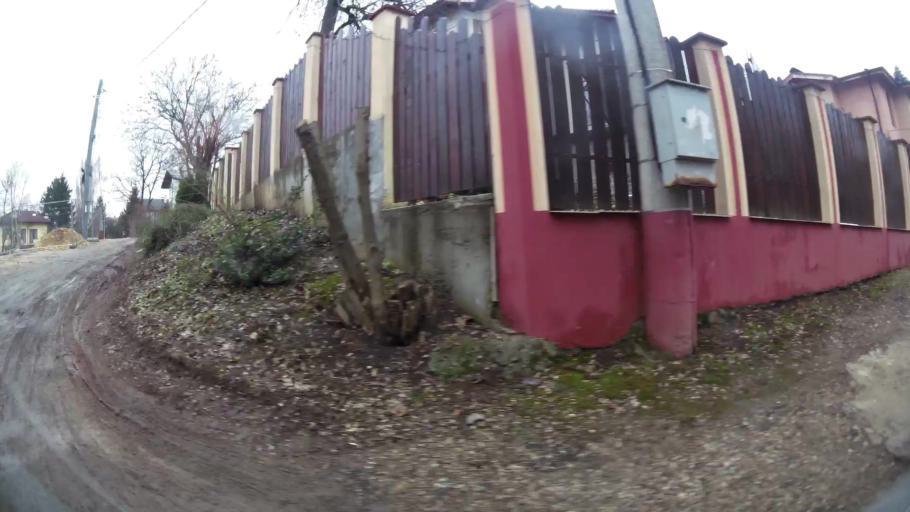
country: BG
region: Sofia-Capital
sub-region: Stolichna Obshtina
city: Sofia
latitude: 42.6117
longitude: 23.3661
